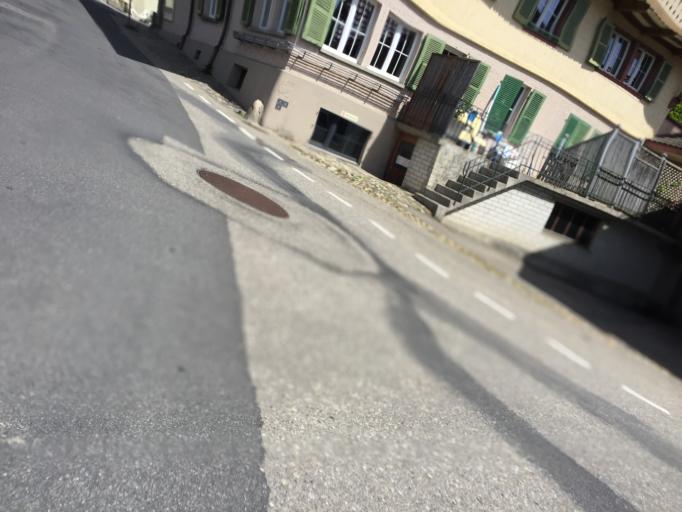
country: CH
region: Bern
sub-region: Emmental District
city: Signau
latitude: 46.9203
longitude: 7.7260
